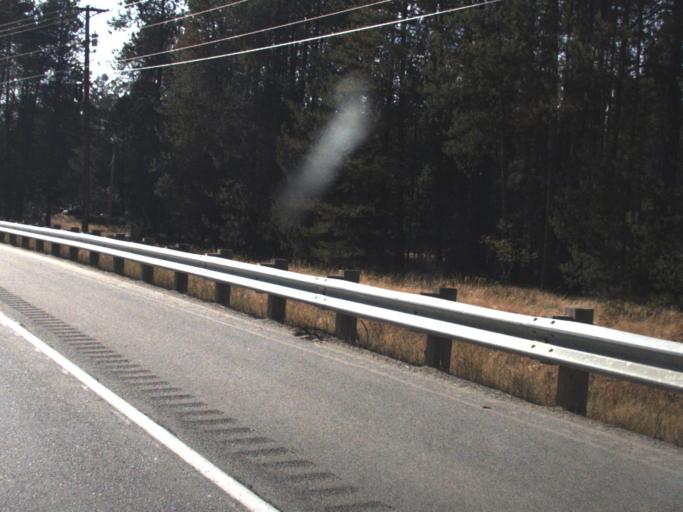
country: US
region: Washington
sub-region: Pend Oreille County
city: Newport
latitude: 48.1476
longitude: -117.1342
